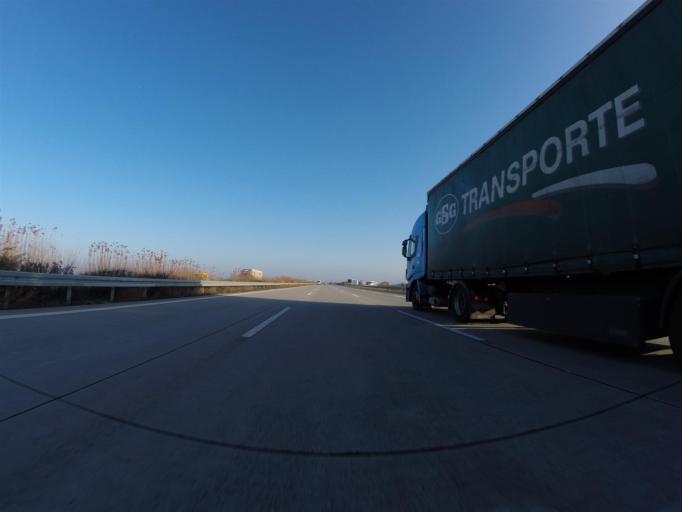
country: DE
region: Saxony
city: Grosslehna
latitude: 51.3226
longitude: 12.1691
